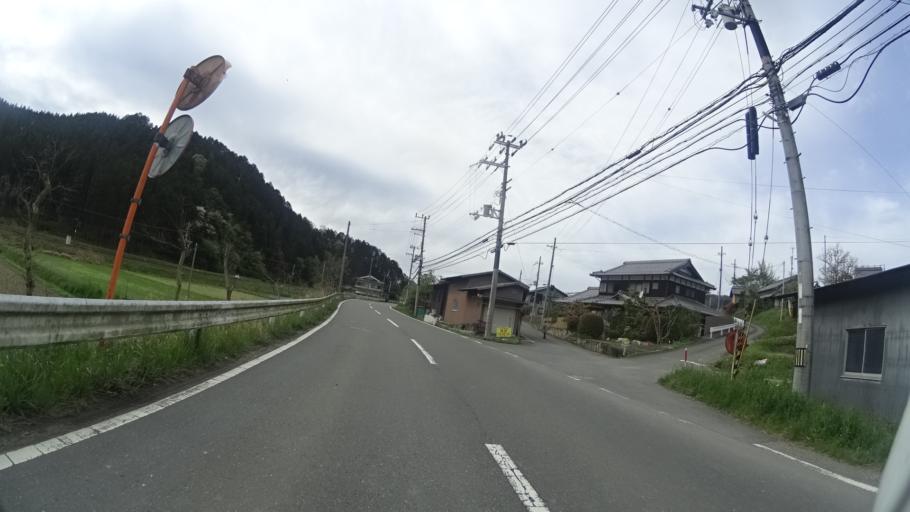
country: JP
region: Kyoto
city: Kameoka
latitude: 35.1907
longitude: 135.4816
